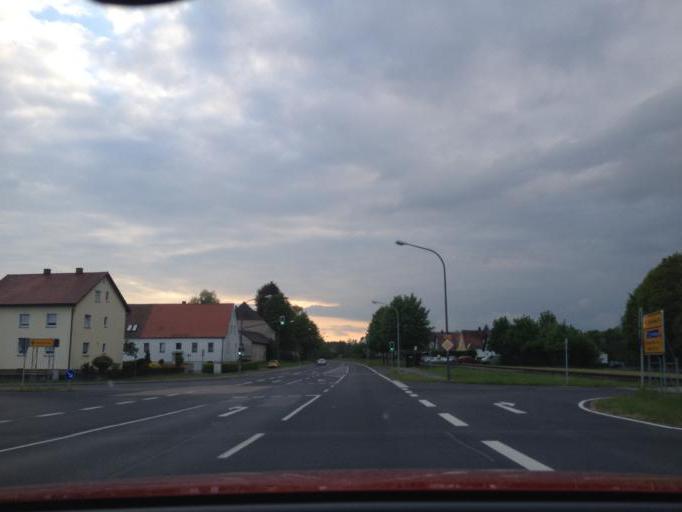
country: DE
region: Bavaria
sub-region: Upper Palatinate
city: Hirschau
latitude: 49.5406
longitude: 11.9360
